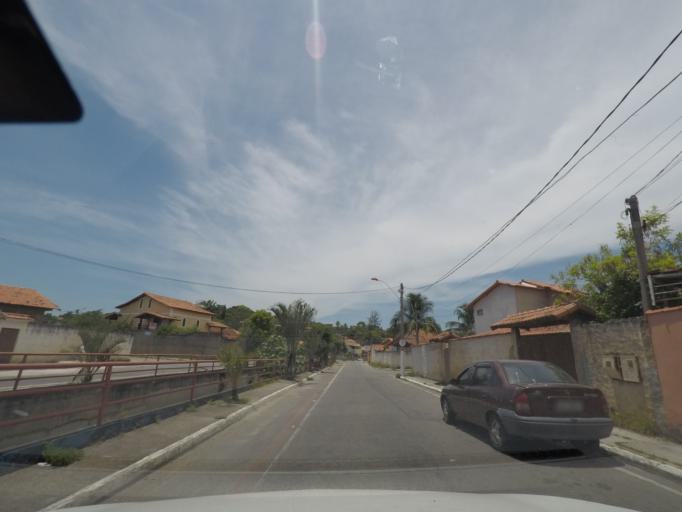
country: BR
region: Rio de Janeiro
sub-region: Marica
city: Marica
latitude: -22.9235
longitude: -42.8205
